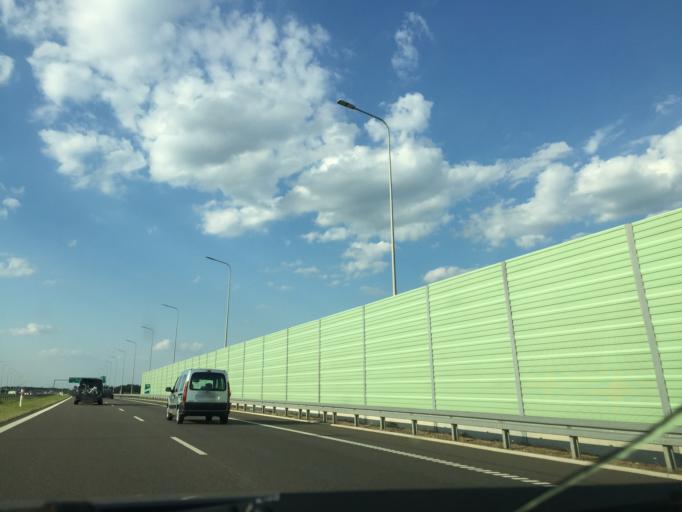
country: PL
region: Masovian Voivodeship
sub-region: Powiat radomski
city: Wolanow
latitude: 51.3813
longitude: 21.0202
